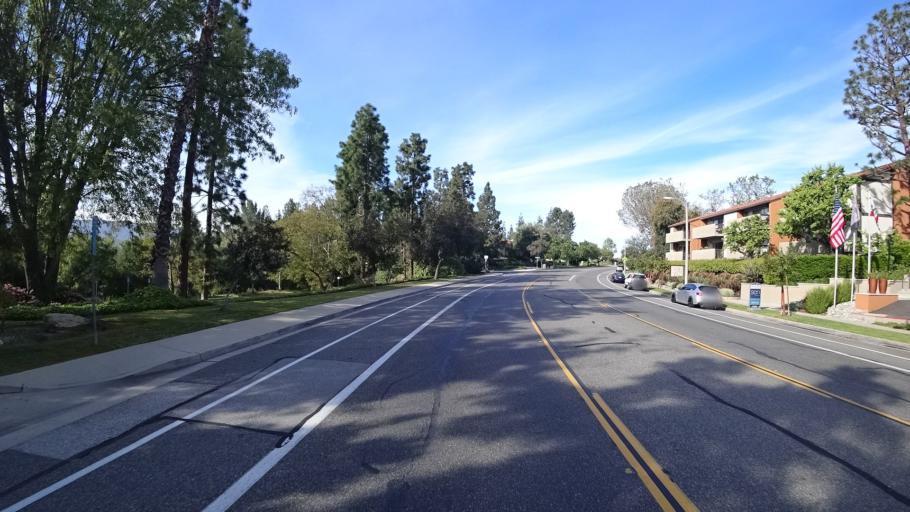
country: US
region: California
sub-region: Ventura County
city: Casa Conejo
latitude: 34.1918
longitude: -118.8892
